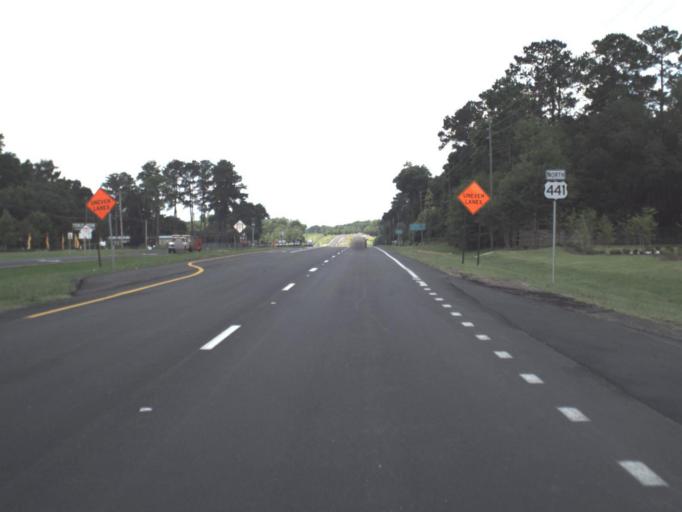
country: US
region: Florida
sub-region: Alachua County
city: Alachua
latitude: 29.7686
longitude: -82.4215
